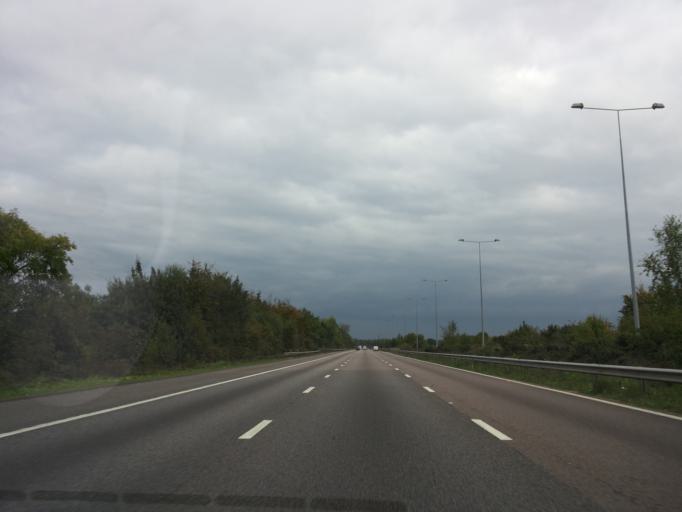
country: GB
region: England
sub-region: Kent
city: Boxley
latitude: 51.3256
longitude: 0.5409
